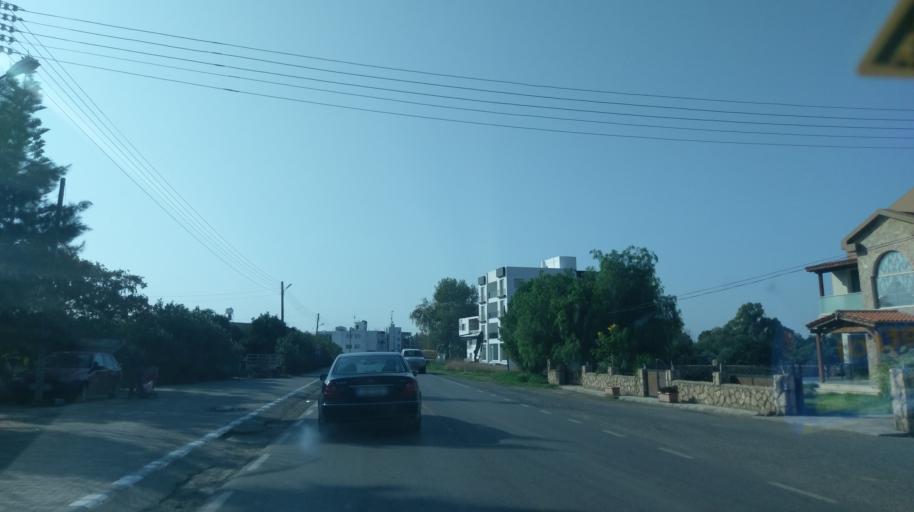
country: CY
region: Lefkosia
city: Lefka
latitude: 35.1541
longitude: 32.8731
